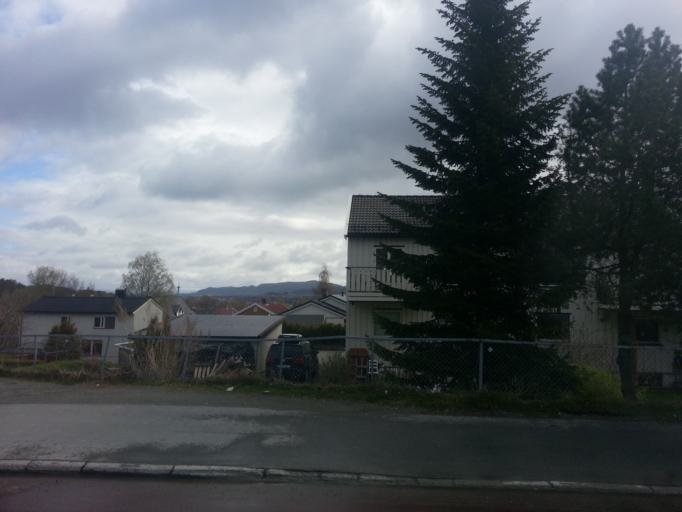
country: NO
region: Sor-Trondelag
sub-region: Trondheim
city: Trondheim
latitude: 63.4164
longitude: 10.3531
